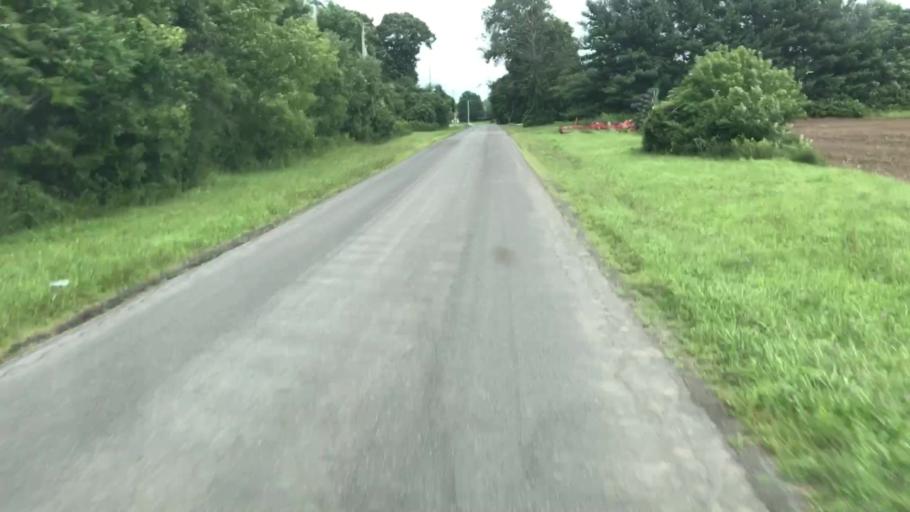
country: US
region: New York
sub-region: Onondaga County
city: Elbridge
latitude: 42.9980
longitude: -76.4430
